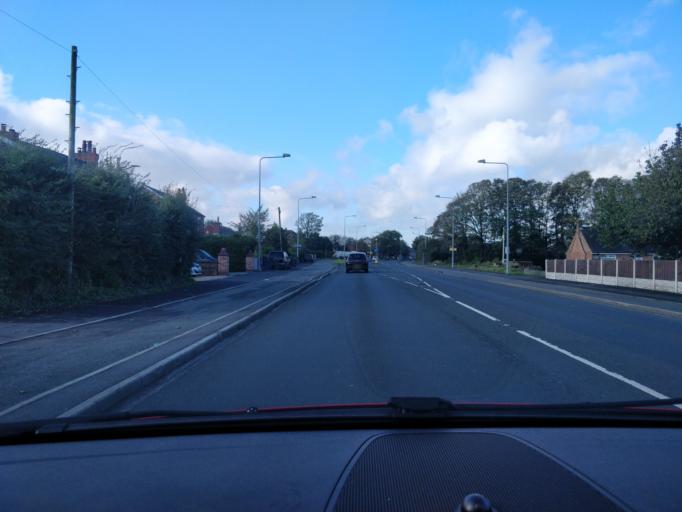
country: GB
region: England
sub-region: Sefton
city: Southport
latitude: 53.6229
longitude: -2.9593
